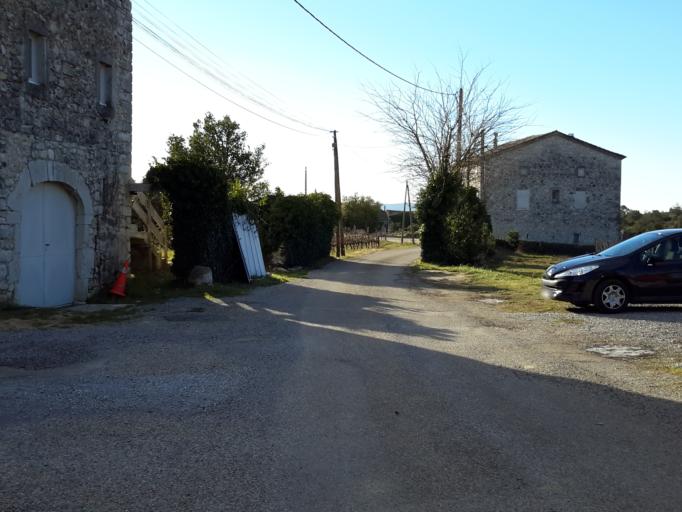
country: FR
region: Rhone-Alpes
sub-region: Departement de l'Ardeche
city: Lavilledieu
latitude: 44.5532
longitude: 4.4349
